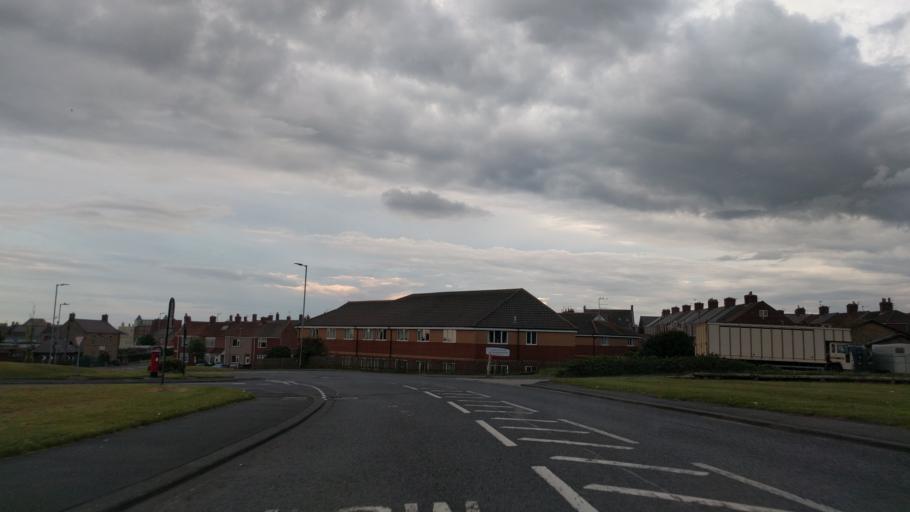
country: GB
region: England
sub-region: Northumberland
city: Newbiggin-by-the-Sea
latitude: 55.1862
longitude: -1.5155
